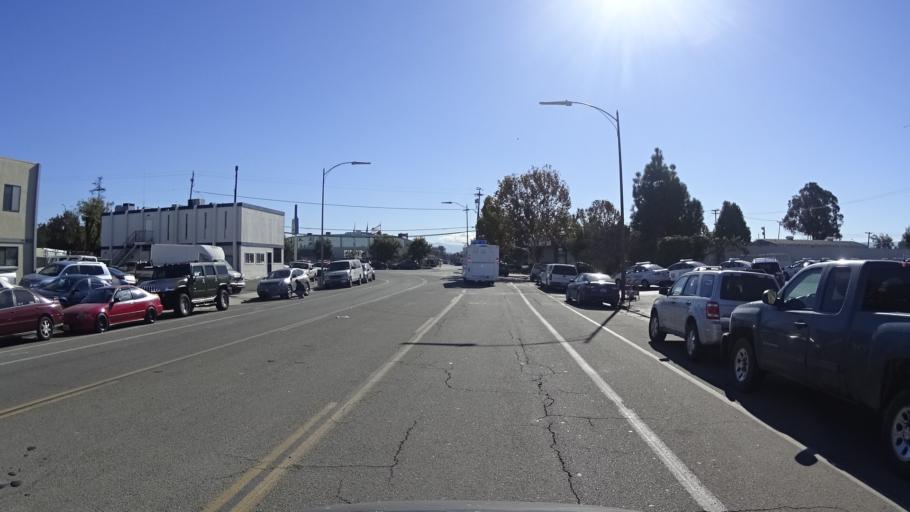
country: US
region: California
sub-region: Santa Clara County
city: San Jose
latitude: 37.3704
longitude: -121.8974
